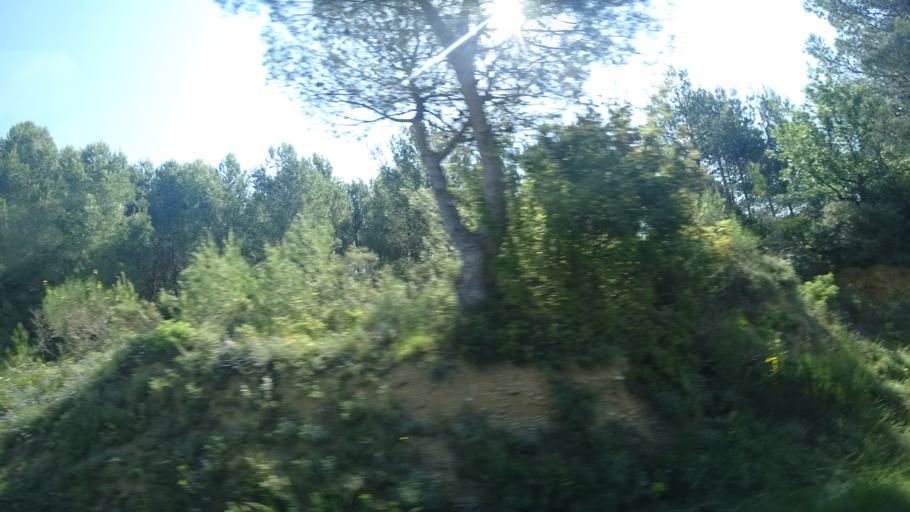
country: FR
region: Languedoc-Roussillon
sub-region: Departement de l'Herault
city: Olonzac
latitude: 43.3352
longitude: 2.7337
